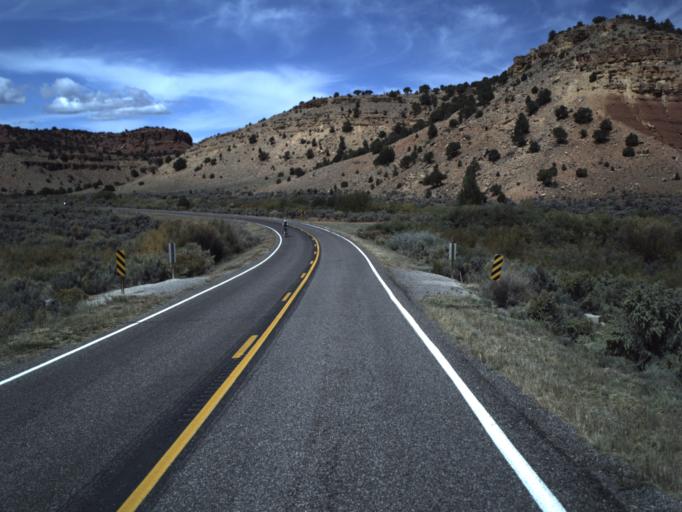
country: US
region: Utah
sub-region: Wayne County
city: Loa
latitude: 38.2696
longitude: -111.3755
